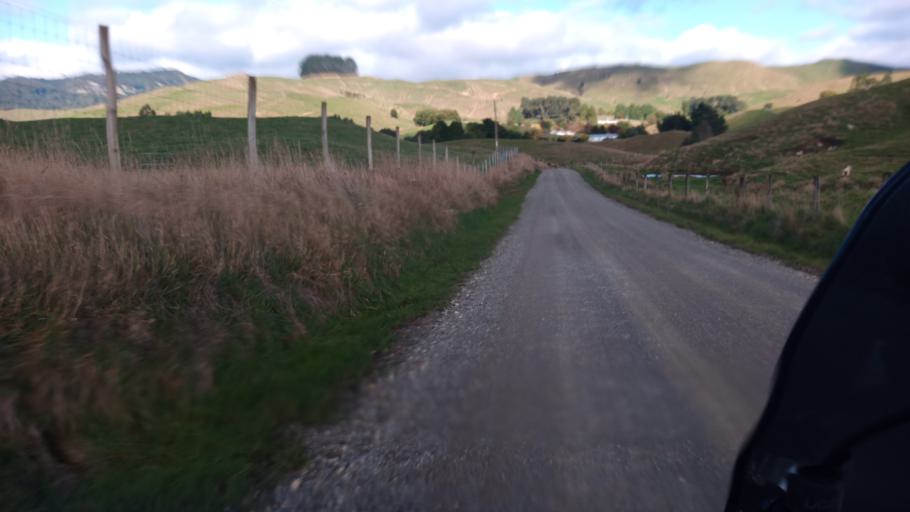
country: NZ
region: Bay of Plenty
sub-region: Opotiki District
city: Opotiki
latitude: -38.4580
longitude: 177.3905
